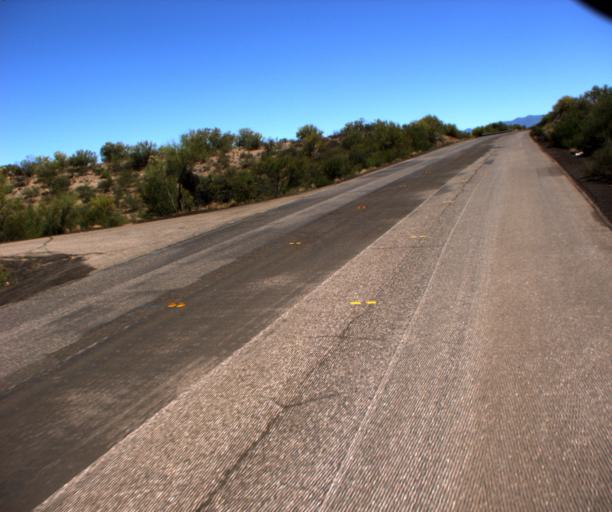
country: US
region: Arizona
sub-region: Pinal County
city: Mammoth
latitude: 32.6836
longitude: -110.6539
